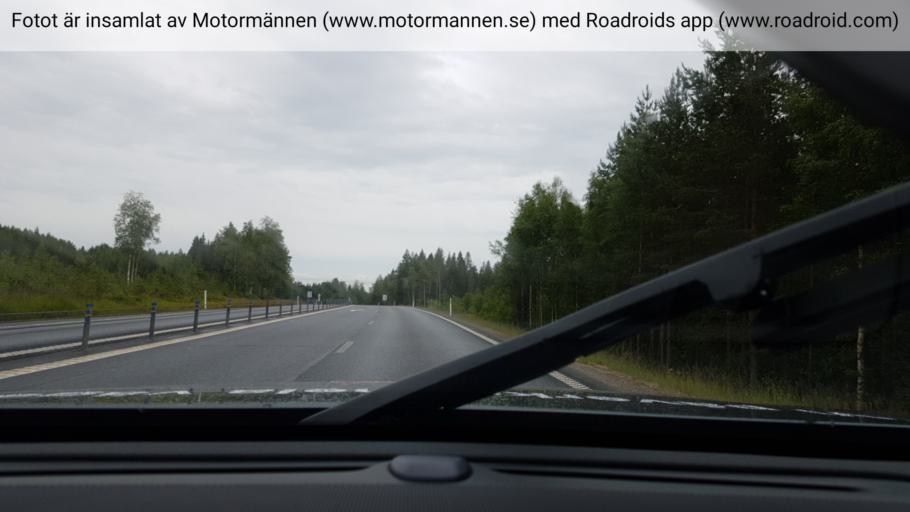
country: SE
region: Vaesterbotten
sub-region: Vannas Kommun
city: Vannasby
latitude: 63.9054
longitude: 19.8920
